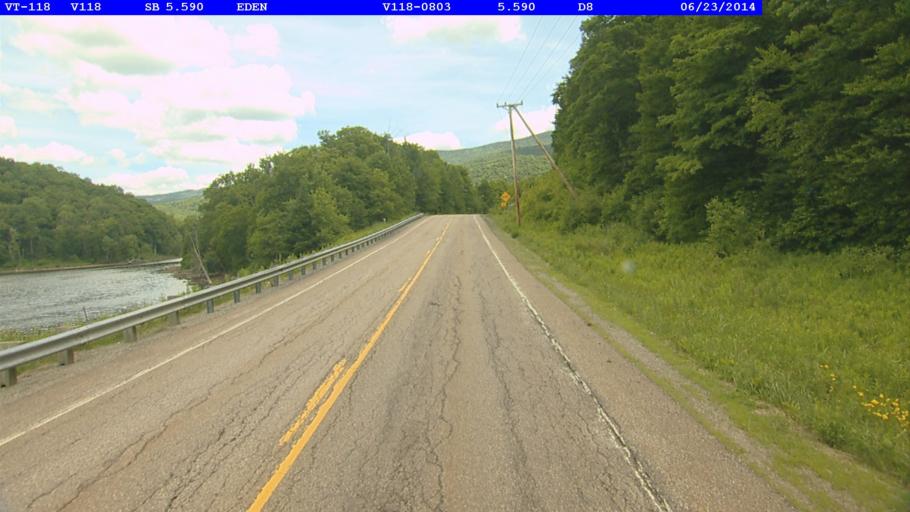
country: US
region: Vermont
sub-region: Lamoille County
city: Johnson
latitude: 44.7648
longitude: -72.6054
